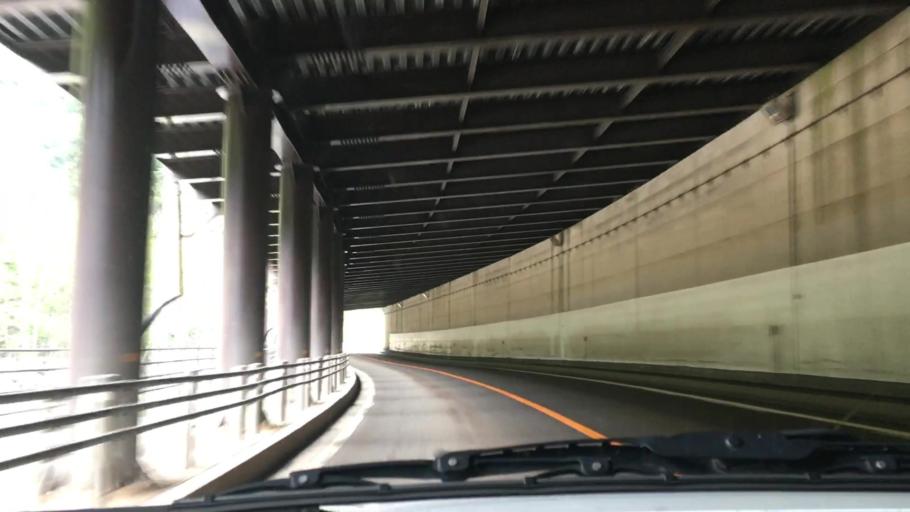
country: JP
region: Hokkaido
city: Otofuke
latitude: 43.3618
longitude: 143.2399
